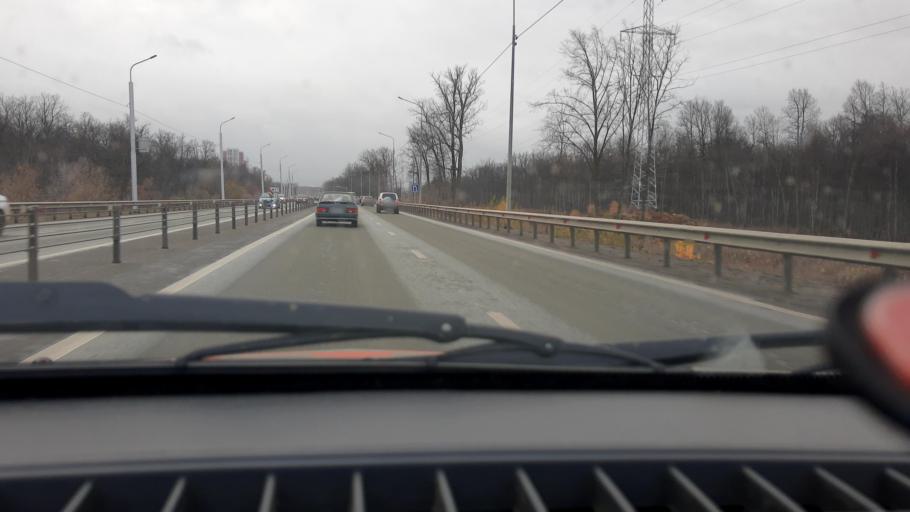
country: RU
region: Bashkortostan
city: Ufa
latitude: 54.6983
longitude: 55.8855
